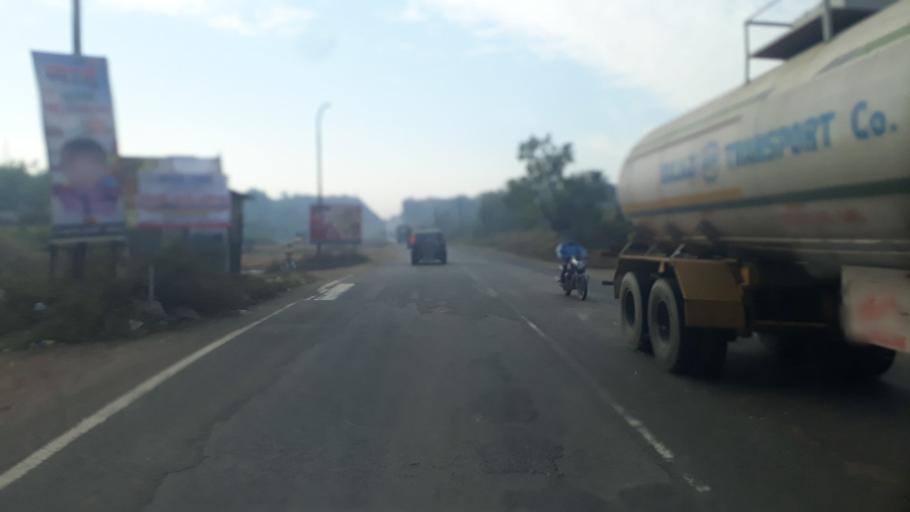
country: IN
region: Maharashtra
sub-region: Raigarh
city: Pen
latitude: 18.8317
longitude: 73.0940
